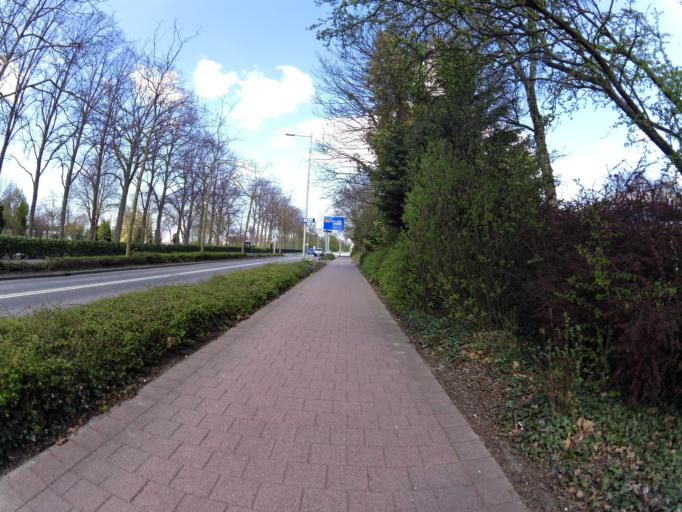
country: NL
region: South Holland
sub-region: Gemeente Brielle
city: Brielle
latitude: 51.8976
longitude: 4.1598
